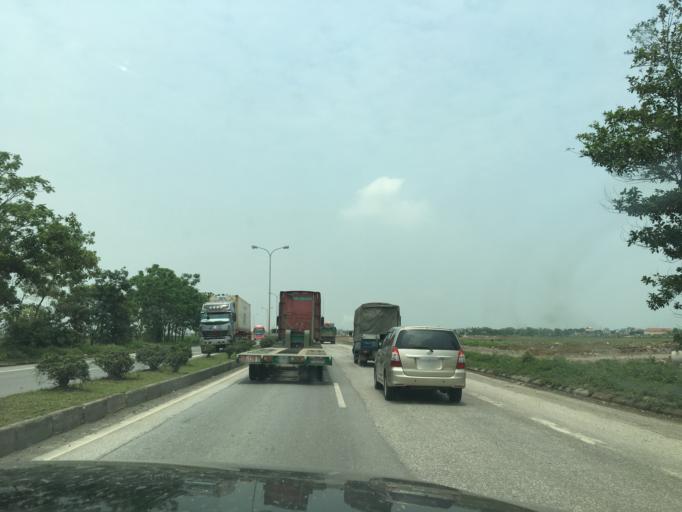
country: VN
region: Ninh Binh
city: Thanh Pho Ninh Binh
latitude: 20.2173
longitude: 105.9867
